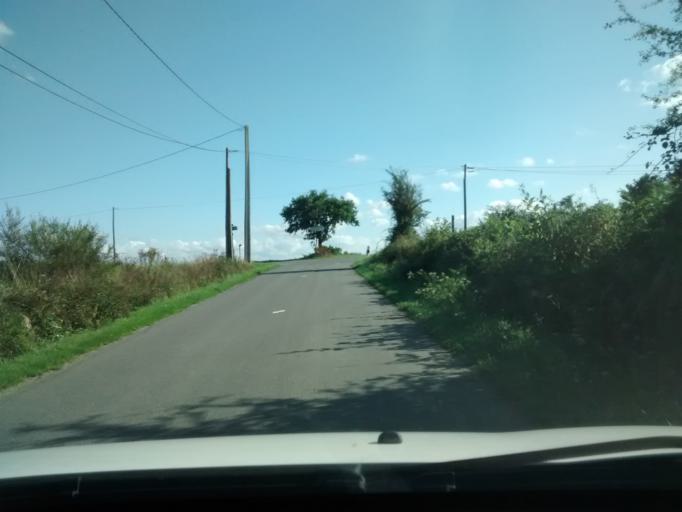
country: FR
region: Brittany
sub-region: Departement d'Ille-et-Vilaine
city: Chantepie
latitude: 48.0882
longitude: -1.5833
